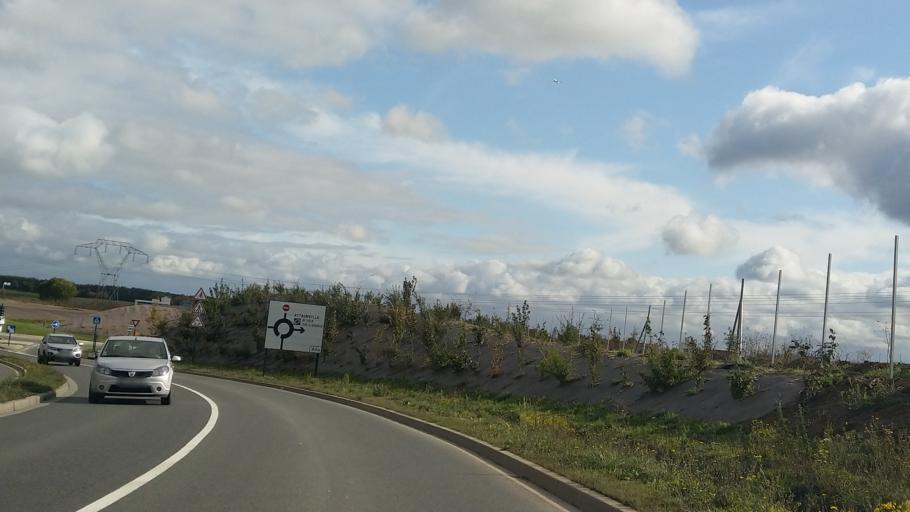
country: FR
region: Ile-de-France
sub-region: Departement du Val-d'Oise
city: Attainville
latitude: 49.0629
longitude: 2.3367
